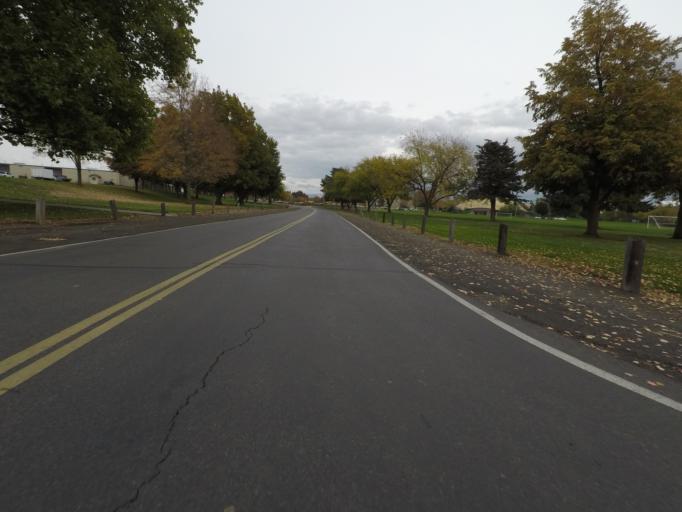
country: US
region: Washington
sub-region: Walla Walla County
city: Walla Walla East
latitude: 46.0791
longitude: -118.2829
